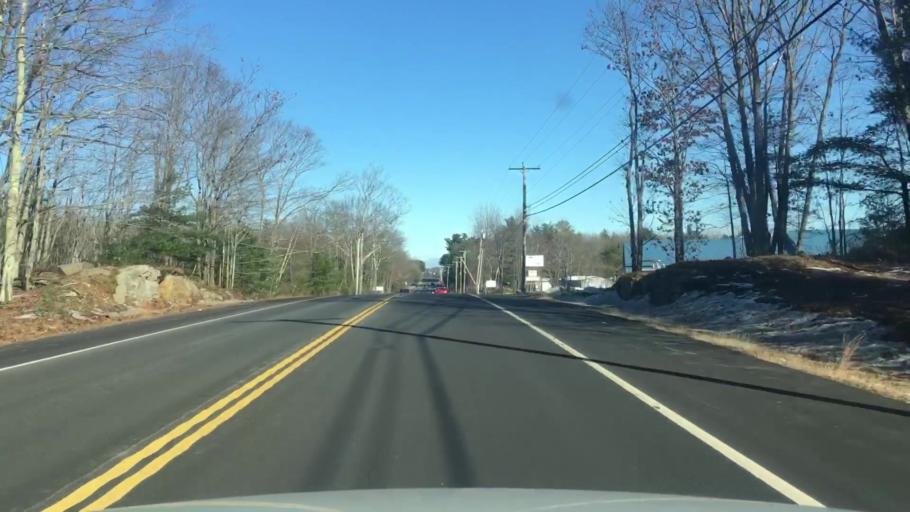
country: US
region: Maine
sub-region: York County
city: Biddeford
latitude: 43.4475
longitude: -70.4994
